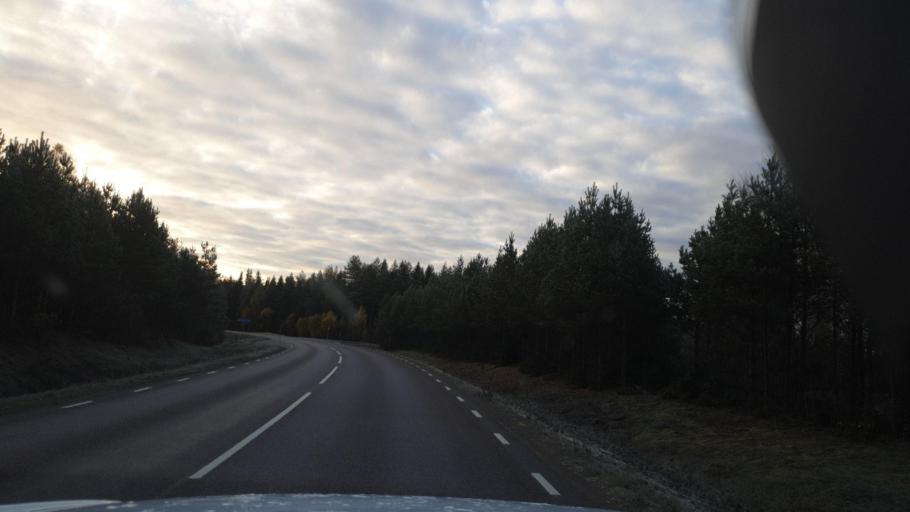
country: SE
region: Vaermland
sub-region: Eda Kommun
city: Amotfors
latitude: 59.7319
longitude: 12.1707
